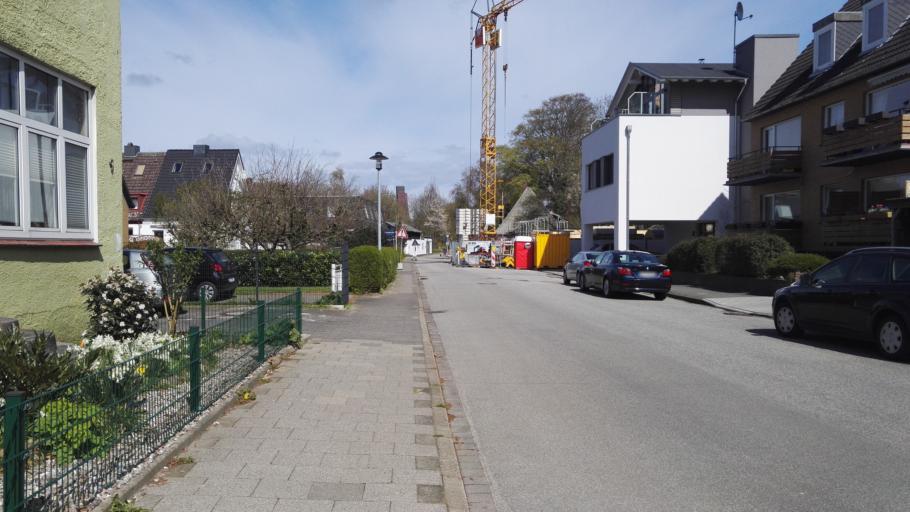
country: DE
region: Schleswig-Holstein
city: Laboe
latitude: 54.4051
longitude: 10.2225
